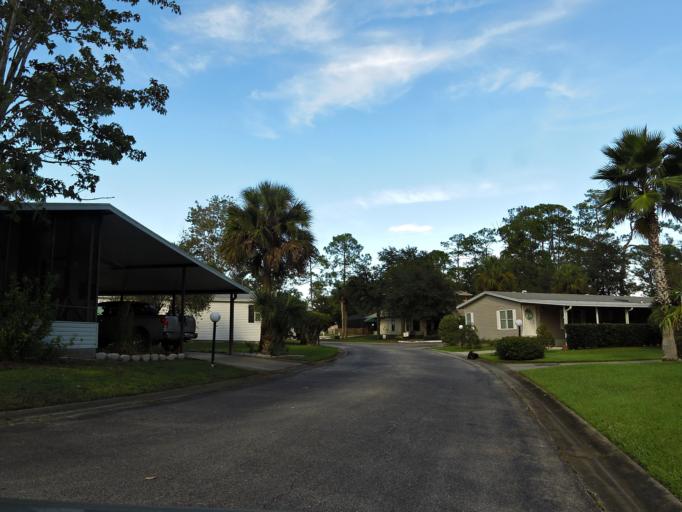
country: US
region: Florida
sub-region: Flagler County
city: Bunnell
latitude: 29.4620
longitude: -81.2623
